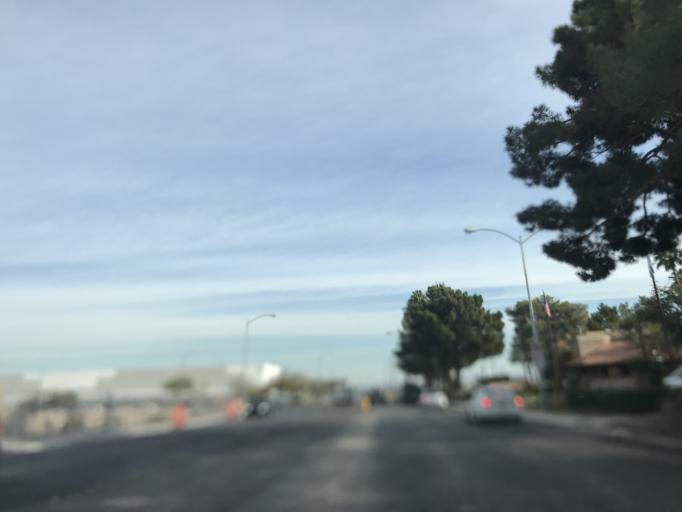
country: US
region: Nevada
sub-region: Clark County
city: Paradise
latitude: 36.0972
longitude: -115.1654
